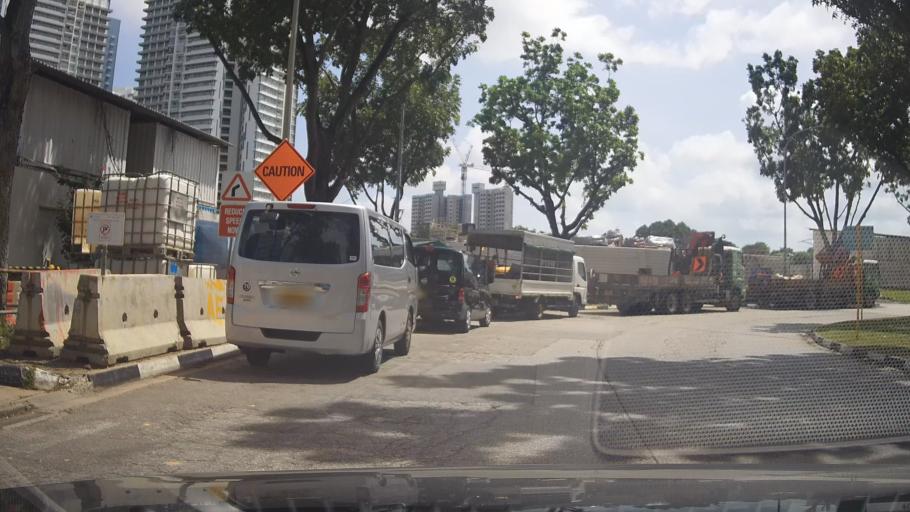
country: SG
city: Singapore
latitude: 1.3118
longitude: 103.8677
